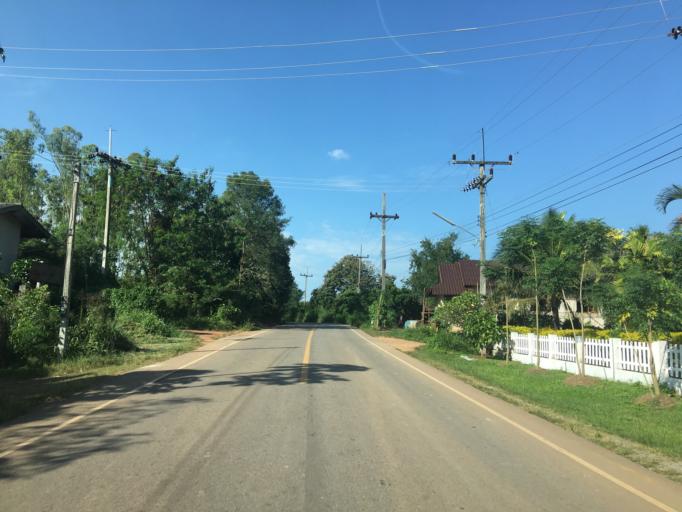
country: TH
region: Chiang Rai
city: Pa Daet
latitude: 19.4282
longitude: 100.0146
